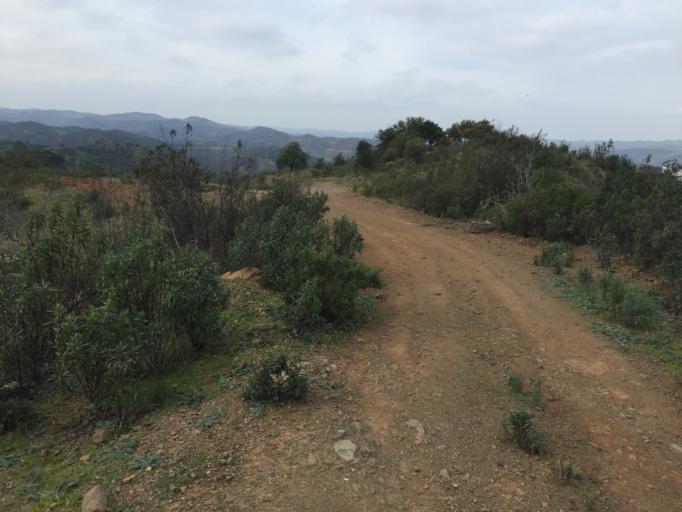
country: PT
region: Faro
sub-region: Tavira
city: Tavira
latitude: 37.3102
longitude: -7.6168
